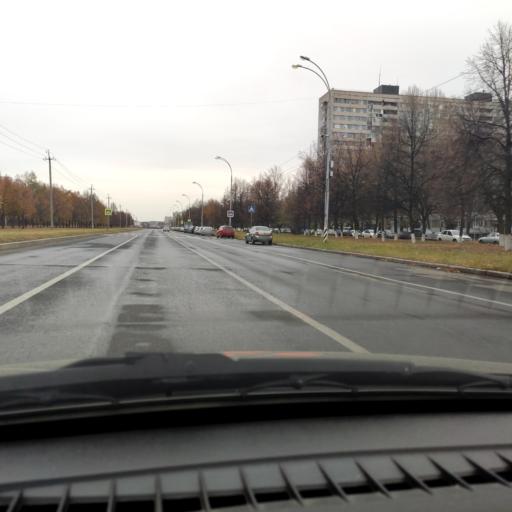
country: RU
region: Samara
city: Tol'yatti
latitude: 53.5210
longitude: 49.2638
